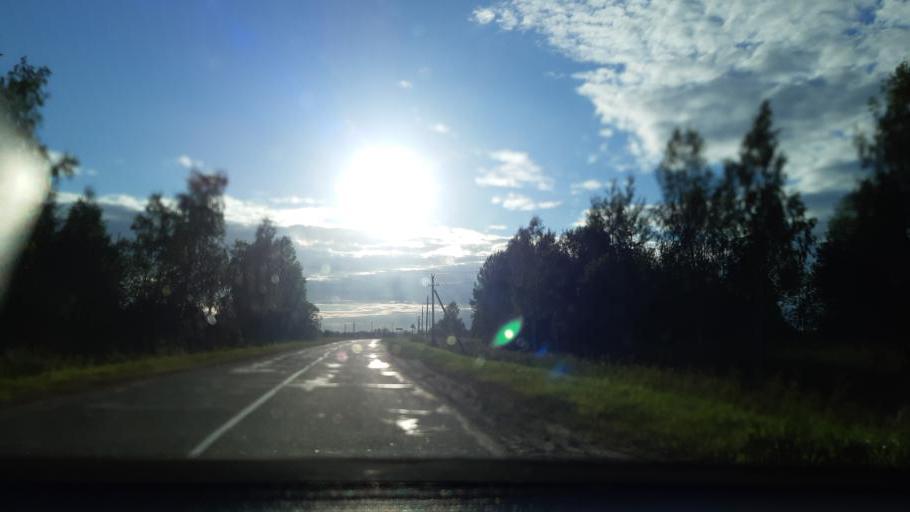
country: RU
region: Smolensk
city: Yel'nya
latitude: 54.5595
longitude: 33.1677
